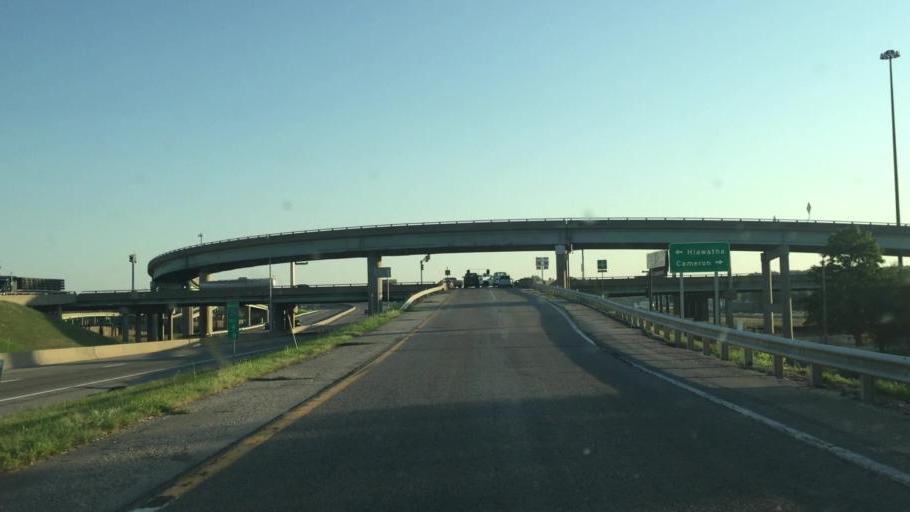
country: US
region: Kansas
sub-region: Doniphan County
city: Elwood
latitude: 39.7474
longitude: -94.8533
